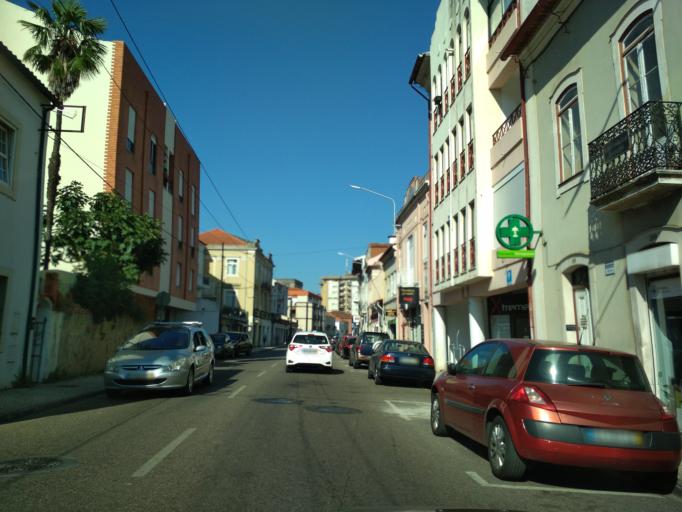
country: PT
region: Coimbra
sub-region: Coimbra
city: Coimbra
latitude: 40.2013
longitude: -8.4169
